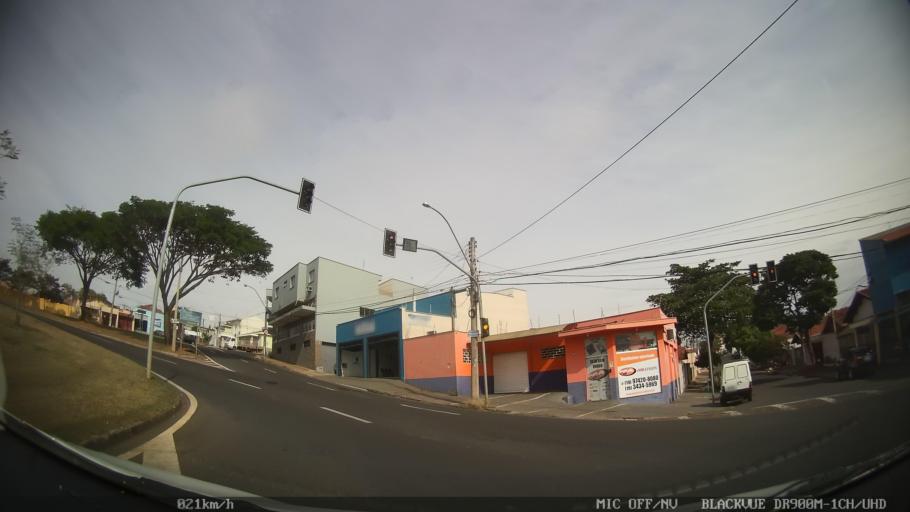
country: BR
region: Sao Paulo
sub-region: Piracicaba
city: Piracicaba
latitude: -22.7336
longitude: -47.6599
